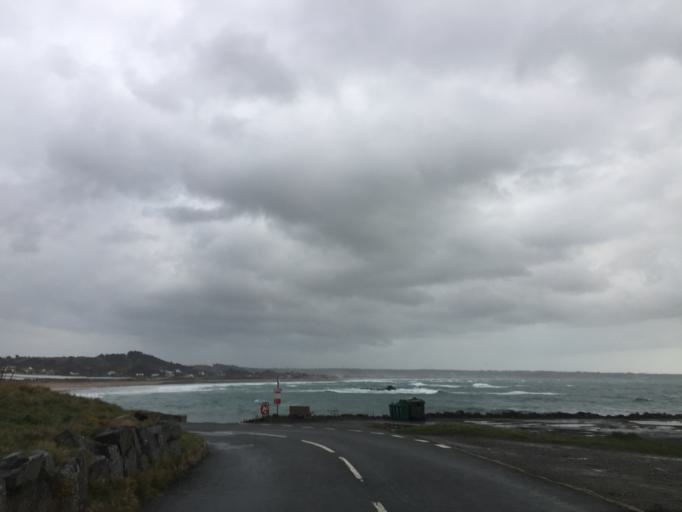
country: JE
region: St Helier
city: Saint Helier
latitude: 49.2408
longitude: -2.2497
